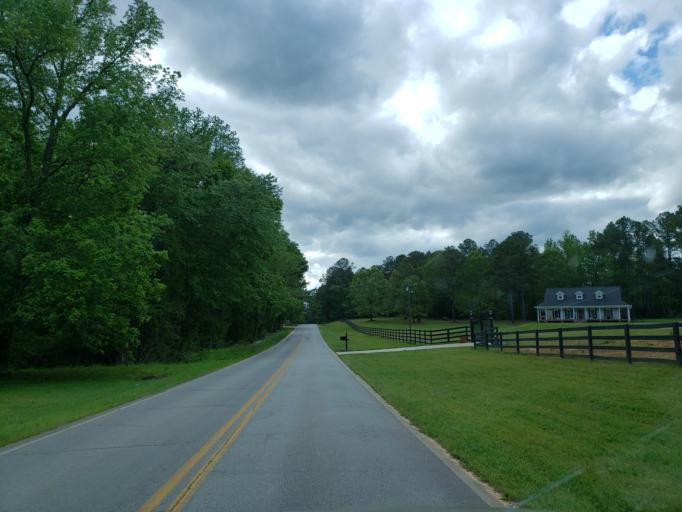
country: US
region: Georgia
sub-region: Haralson County
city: Tallapoosa
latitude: 33.7588
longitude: -85.3114
